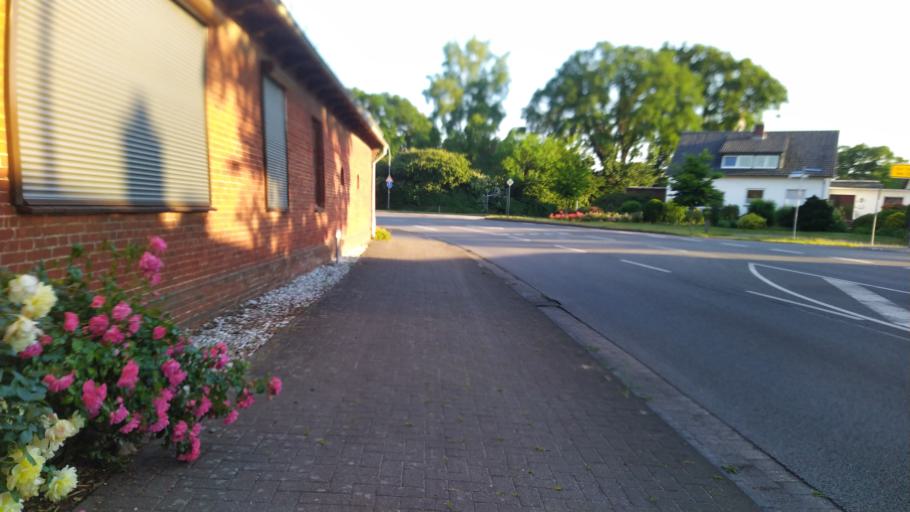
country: DE
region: Lower Saxony
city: Ebersdorf
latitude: 53.5265
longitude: 9.0524
